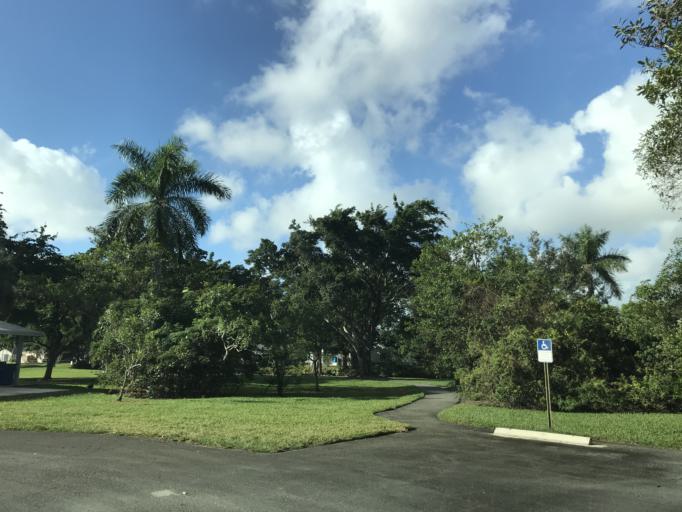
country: US
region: Florida
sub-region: Broward County
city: Coconut Creek
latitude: 26.2629
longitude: -80.1917
